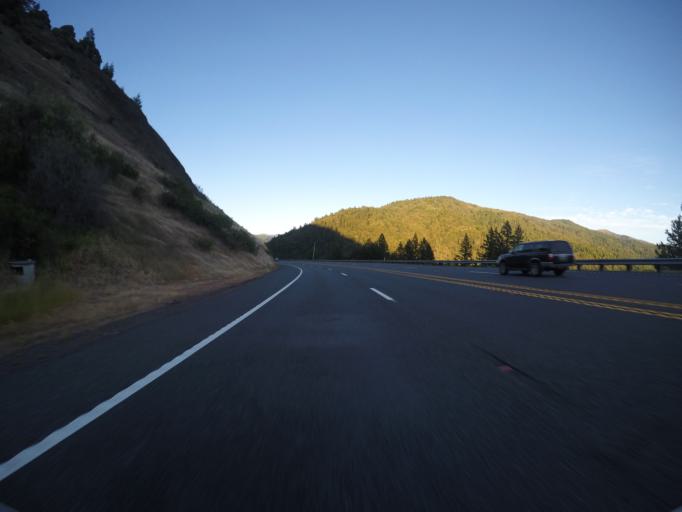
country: US
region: California
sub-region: Mendocino County
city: Laytonville
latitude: 39.8286
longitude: -123.6558
